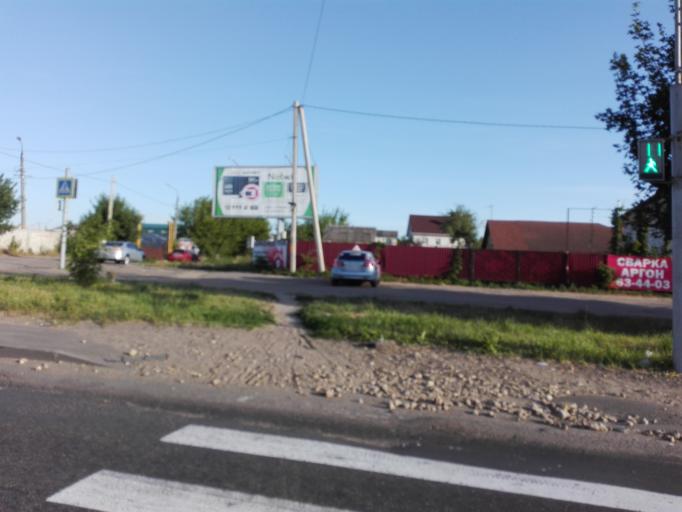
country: RU
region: Orjol
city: Orel
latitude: 52.9470
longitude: 36.0233
